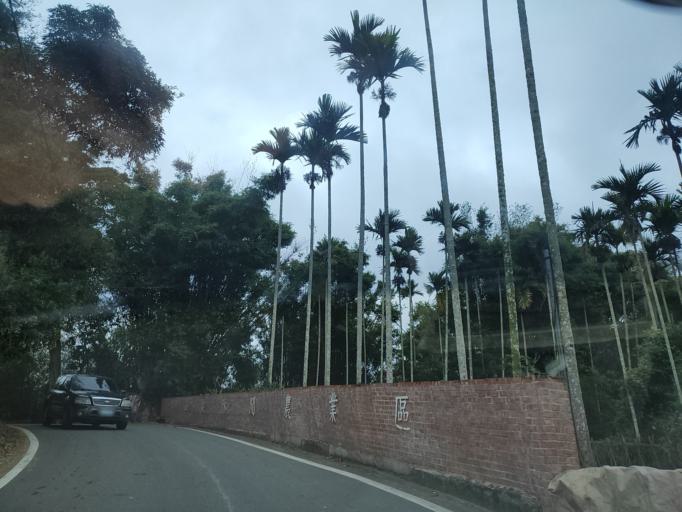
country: TW
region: Taiwan
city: Fengyuan
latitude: 24.3616
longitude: 120.7787
